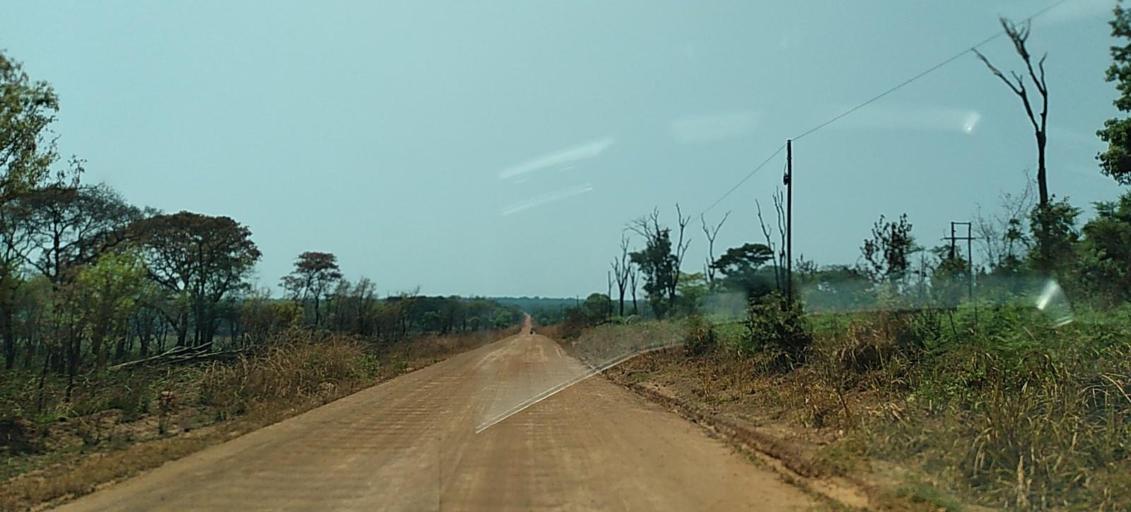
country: ZM
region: North-Western
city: Kansanshi
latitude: -11.9813
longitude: 26.7882
